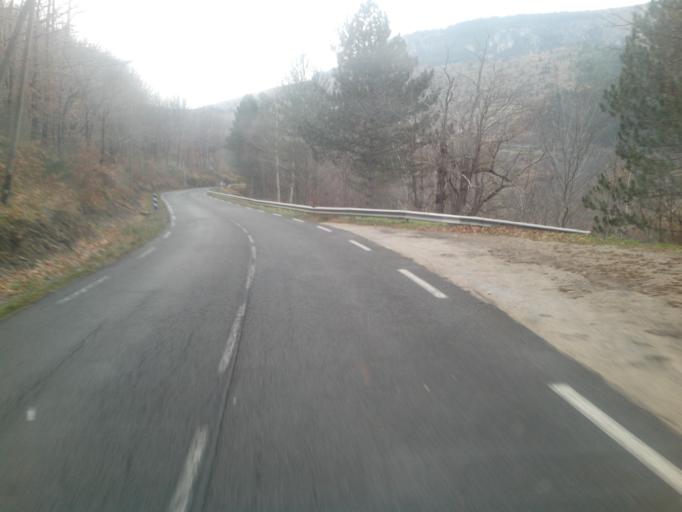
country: FR
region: Languedoc-Roussillon
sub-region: Departement de la Lozere
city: Florac
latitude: 44.3874
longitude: 3.5619
